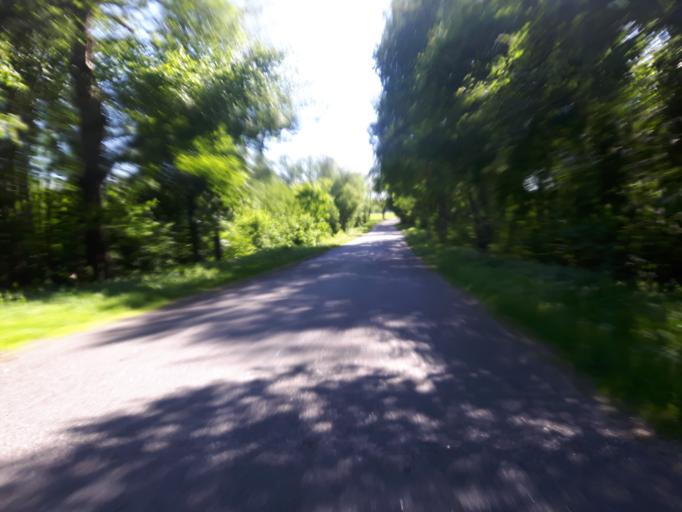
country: EE
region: Laeaene-Virumaa
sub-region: Haljala vald
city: Haljala
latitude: 59.5407
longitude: 26.1050
